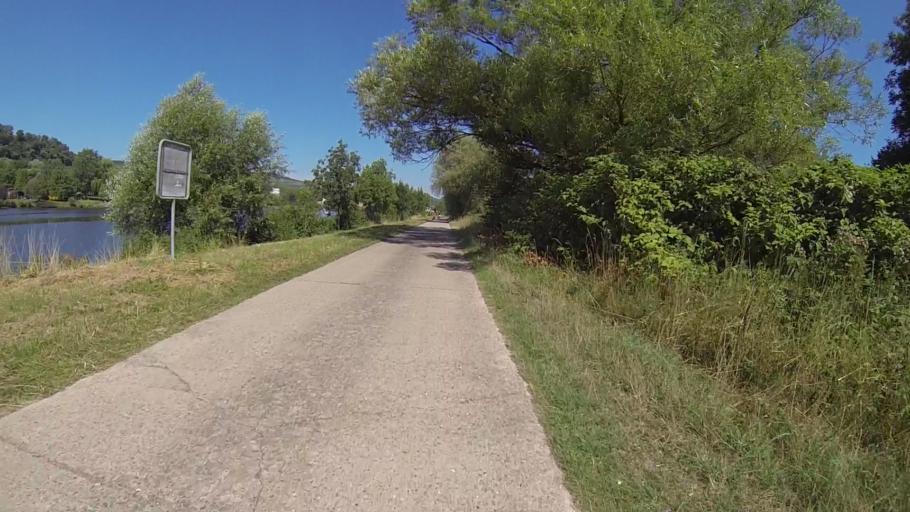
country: LU
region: Grevenmacher
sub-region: Canton de Remich
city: Remich
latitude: 49.5194
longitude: 6.3621
